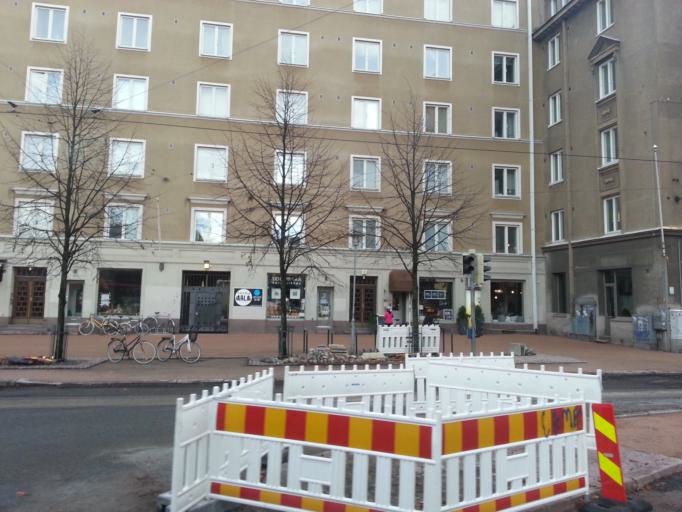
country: FI
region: Uusimaa
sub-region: Helsinki
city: Helsinki
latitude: 60.1866
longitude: 24.9512
